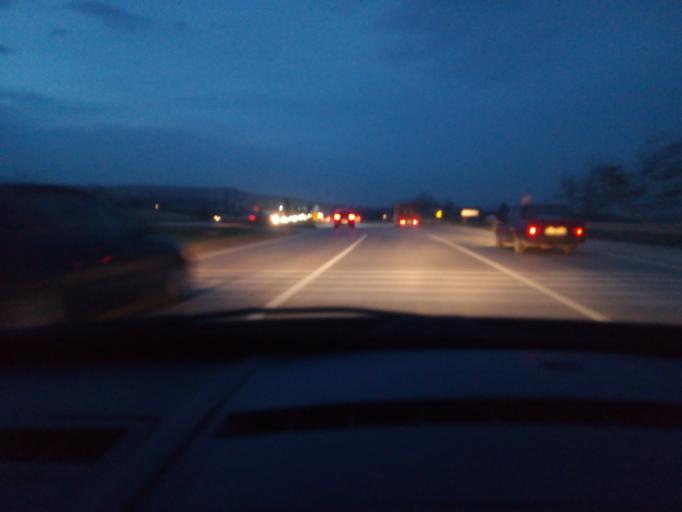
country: TR
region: Balikesir
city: Susurluk
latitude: 39.9556
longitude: 28.1713
